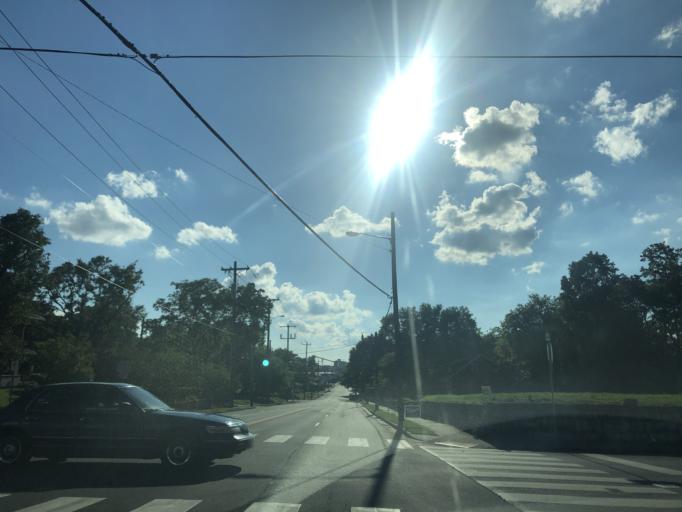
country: US
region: Tennessee
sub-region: Davidson County
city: Nashville
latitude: 36.1870
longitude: -86.7679
